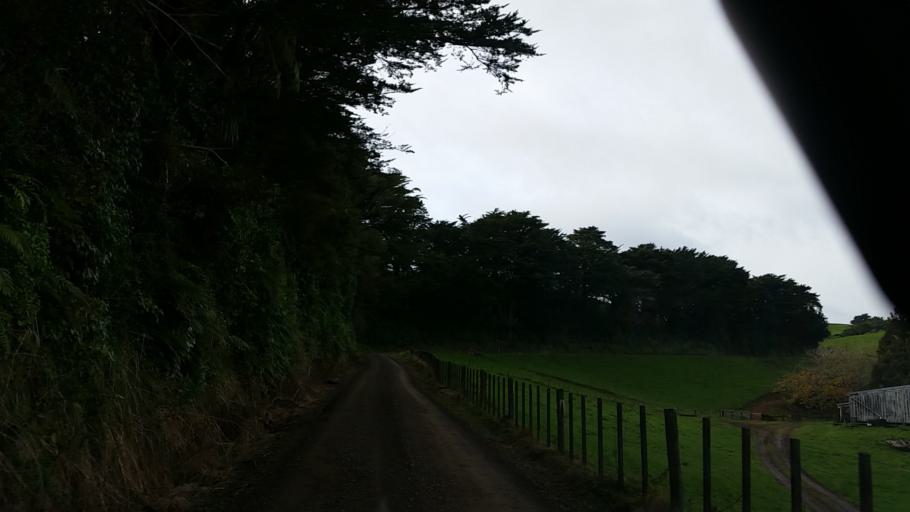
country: NZ
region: Taranaki
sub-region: New Plymouth District
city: Waitara
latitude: -39.0631
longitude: 174.3858
